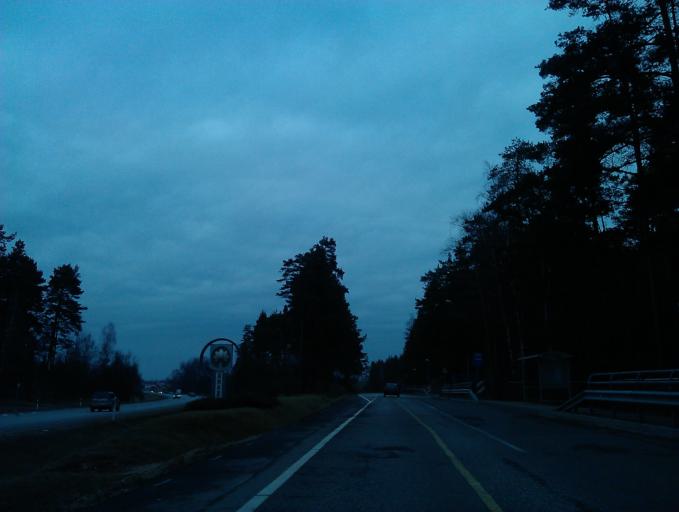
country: LV
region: Adazi
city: Adazi
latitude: 57.0591
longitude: 24.3223
